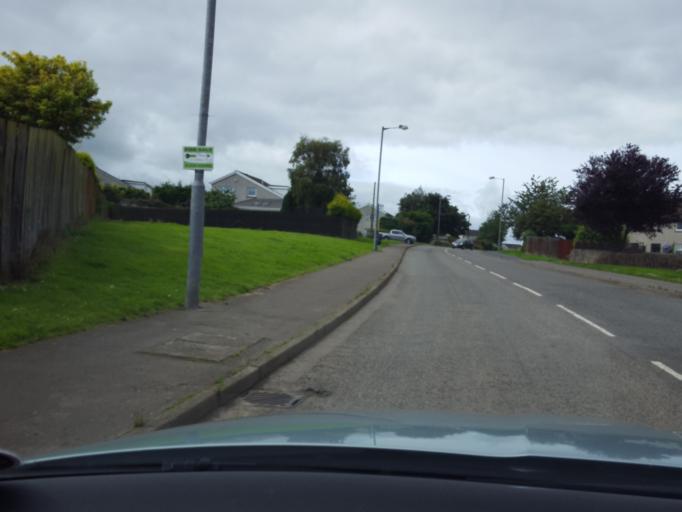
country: GB
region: Scotland
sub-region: Falkirk
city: Bo'ness
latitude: 56.0058
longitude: -3.6031
